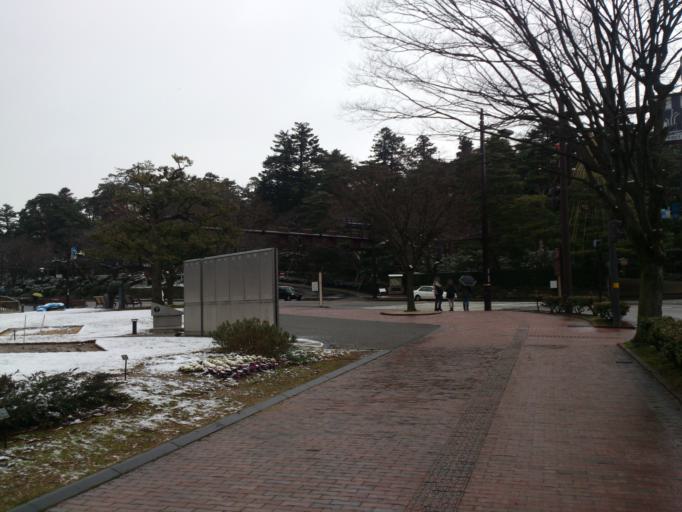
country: JP
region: Ishikawa
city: Kanazawa-shi
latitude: 36.5619
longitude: 136.6590
